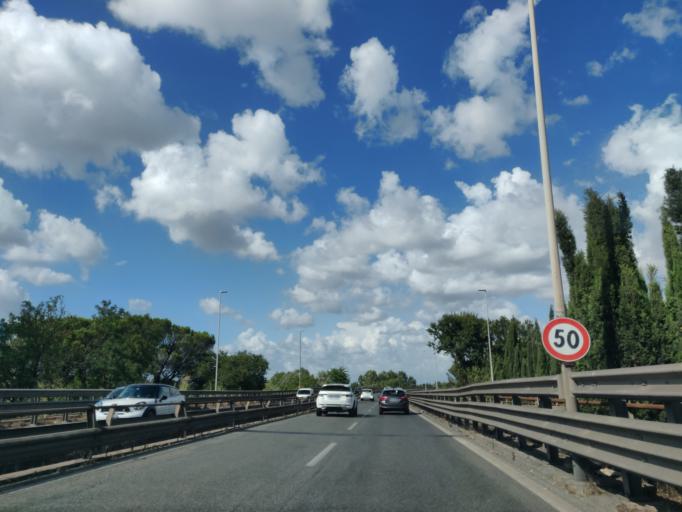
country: VA
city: Vatican City
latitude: 41.8417
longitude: 12.4632
